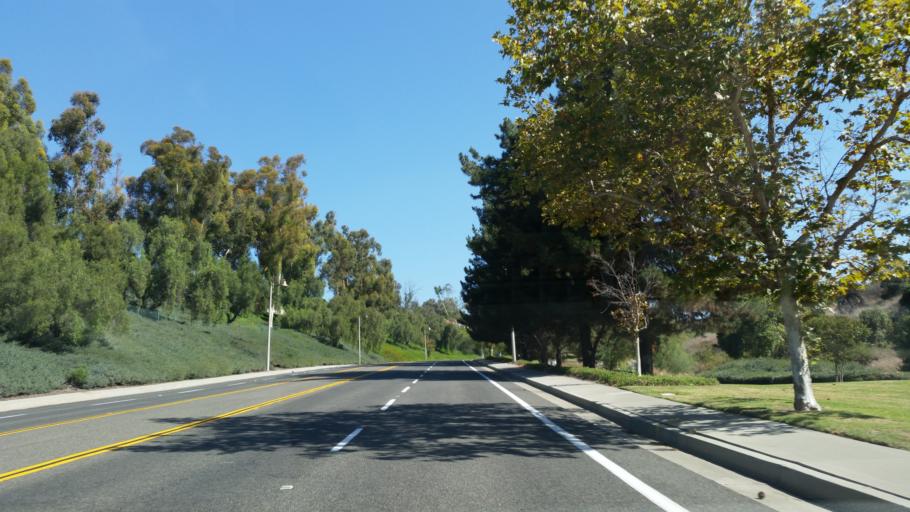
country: US
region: California
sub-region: Orange County
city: Las Flores
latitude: 33.6108
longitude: -117.6429
